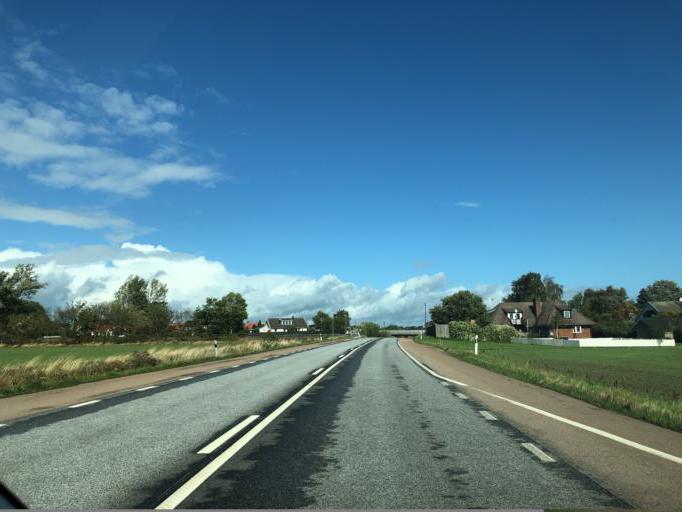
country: SE
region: Skane
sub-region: Helsingborg
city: Glumslov
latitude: 55.9160
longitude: 12.8301
